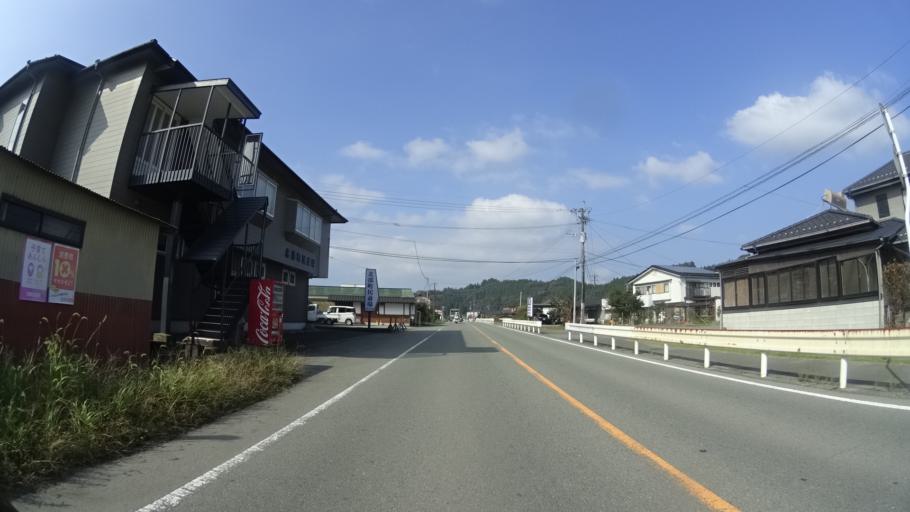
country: JP
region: Kumamoto
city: Aso
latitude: 33.1016
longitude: 131.0678
